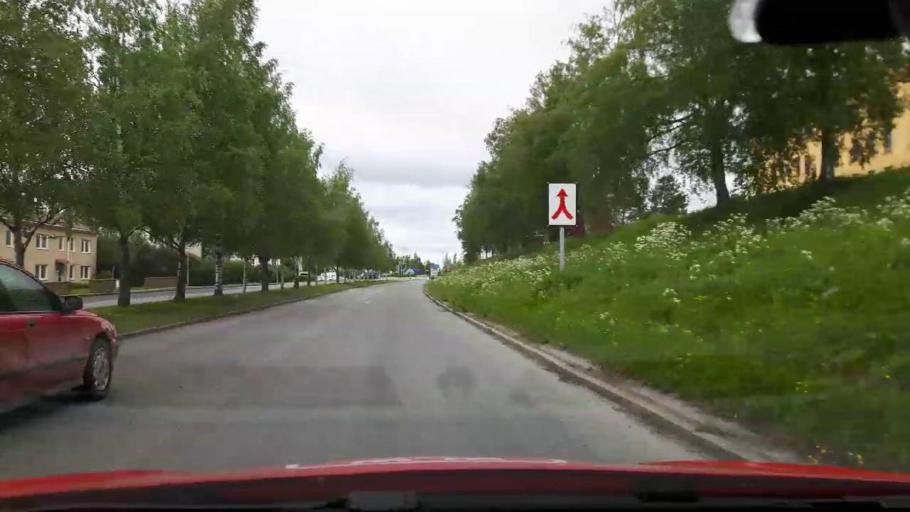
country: SE
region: Jaemtland
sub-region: OEstersunds Kommun
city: Ostersund
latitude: 63.1842
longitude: 14.6396
